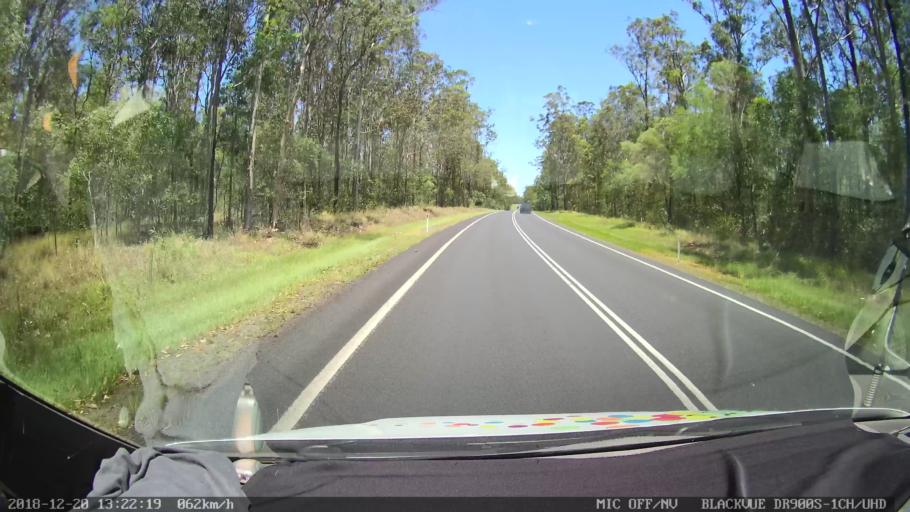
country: AU
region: New South Wales
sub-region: Richmond Valley
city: Casino
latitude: -29.0906
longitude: 153.0015
